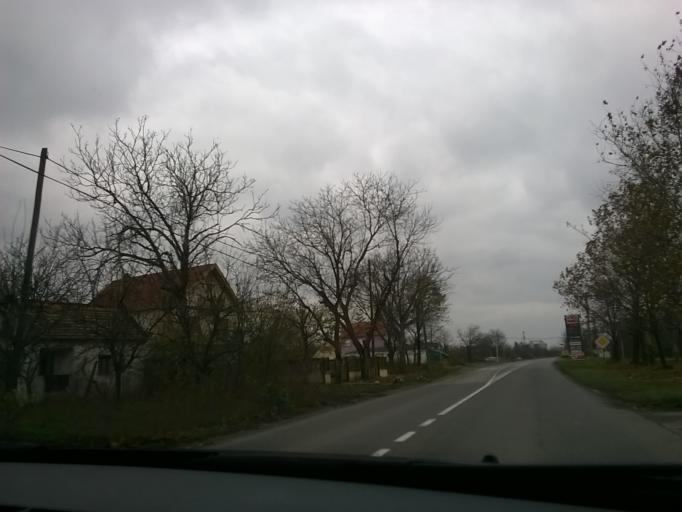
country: RS
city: Centa
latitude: 45.1194
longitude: 20.3867
